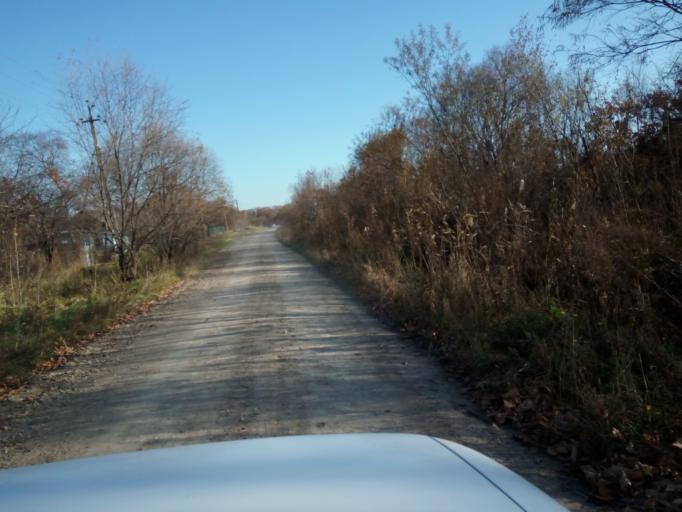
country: RU
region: Primorskiy
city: Lazo
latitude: 45.8752
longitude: 133.6543
